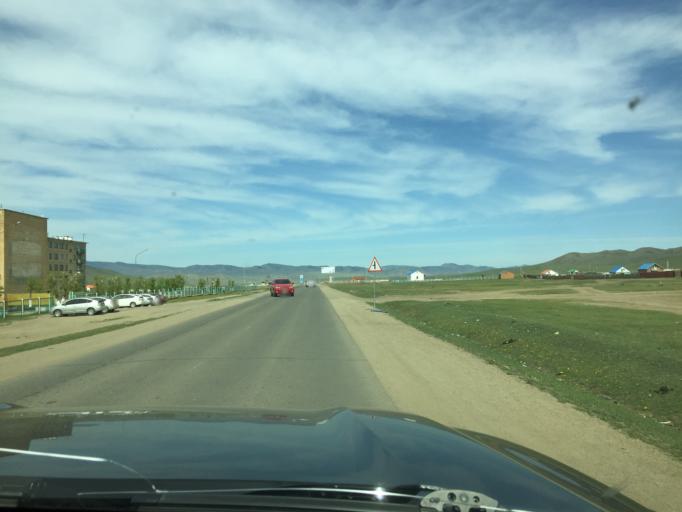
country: MN
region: Central Aimak
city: Ihsueuej
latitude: 48.2264
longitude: 106.2899
